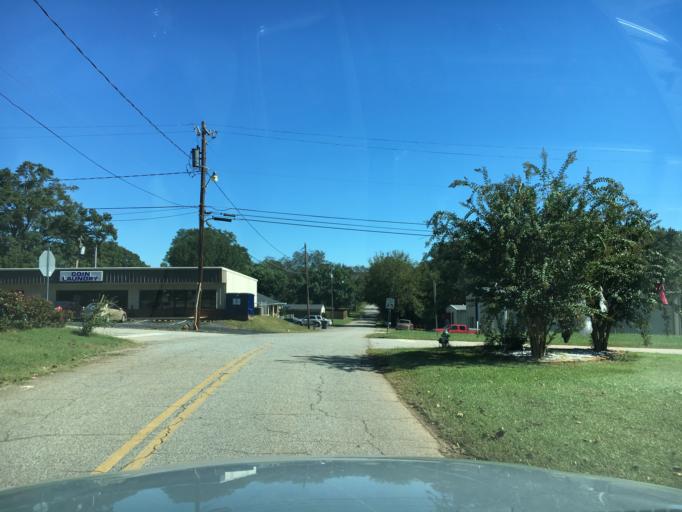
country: US
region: South Carolina
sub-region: Spartanburg County
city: Duncan
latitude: 34.9370
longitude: -82.1402
